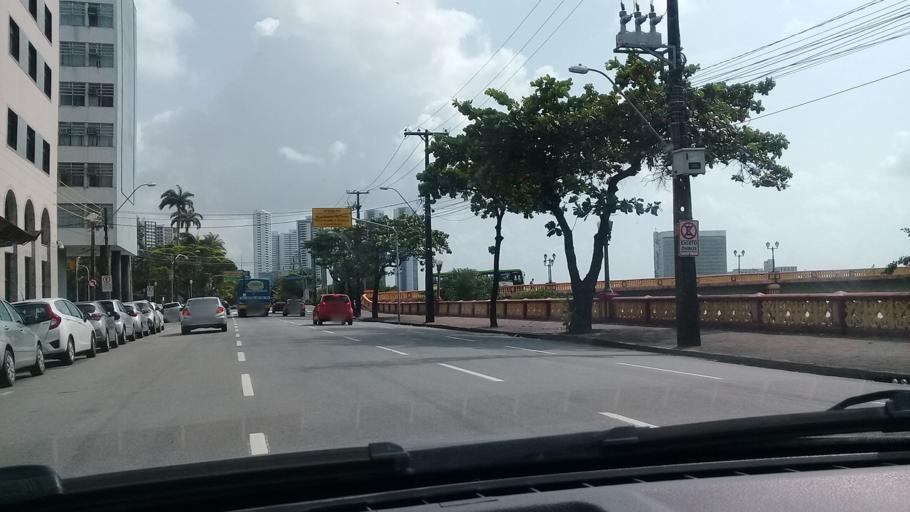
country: BR
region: Pernambuco
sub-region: Recife
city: Recife
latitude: -8.0626
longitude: -34.8764
